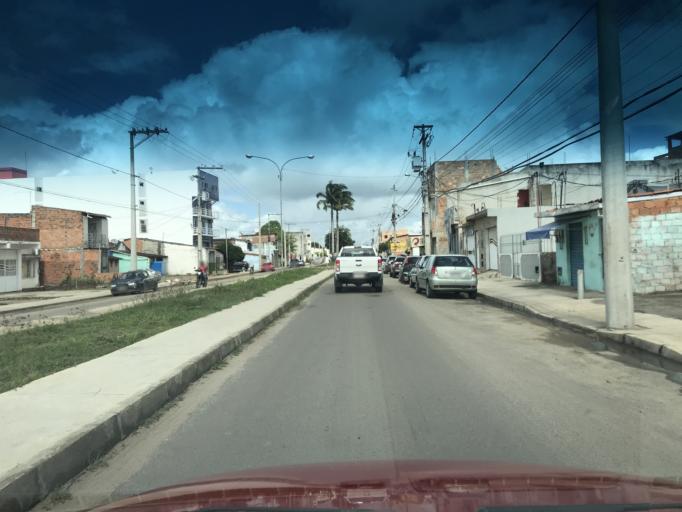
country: BR
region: Bahia
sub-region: Santo Antonio De Jesus
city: Santo Antonio de Jesus
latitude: -12.9707
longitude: -39.2720
